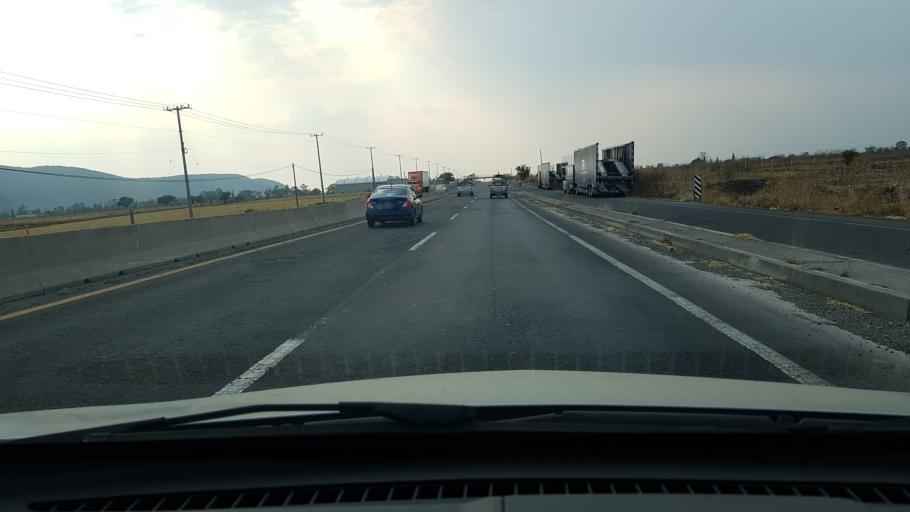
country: MX
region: Morelos
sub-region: Ayala
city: Unidad Habitacional Mariano Matamoros
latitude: 18.7408
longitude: -98.8314
